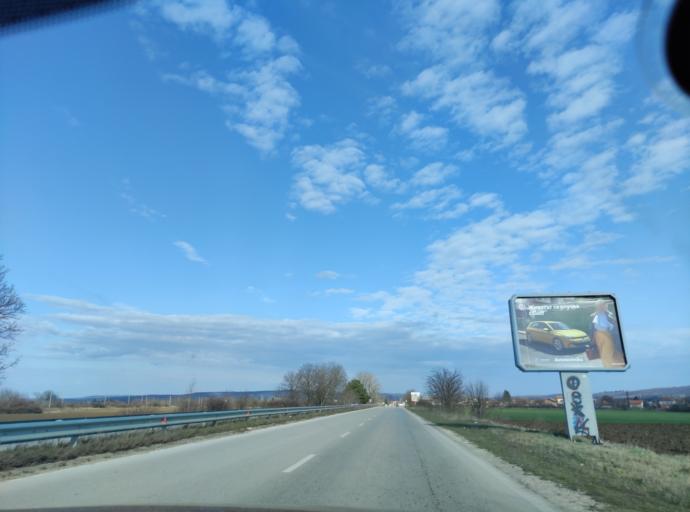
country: BG
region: Pleven
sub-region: Obshtina Dolna Mitropoliya
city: Dolna Mitropoliya
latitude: 43.4279
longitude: 24.5113
